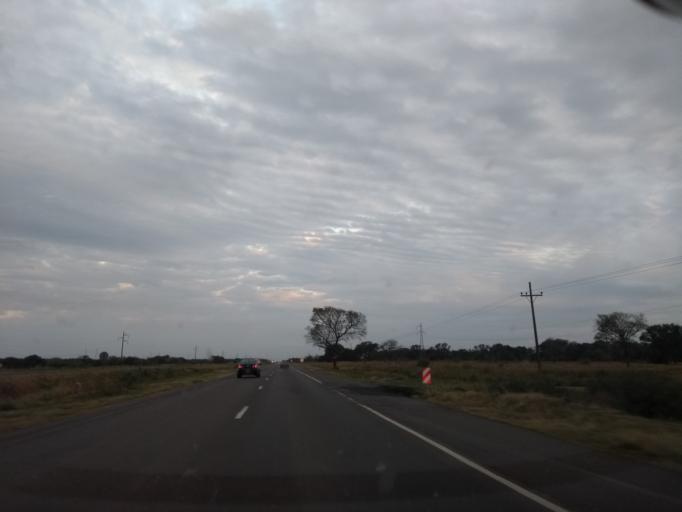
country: AR
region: Chaco
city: Puerto Tirol
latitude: -27.2723
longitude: -59.1423
